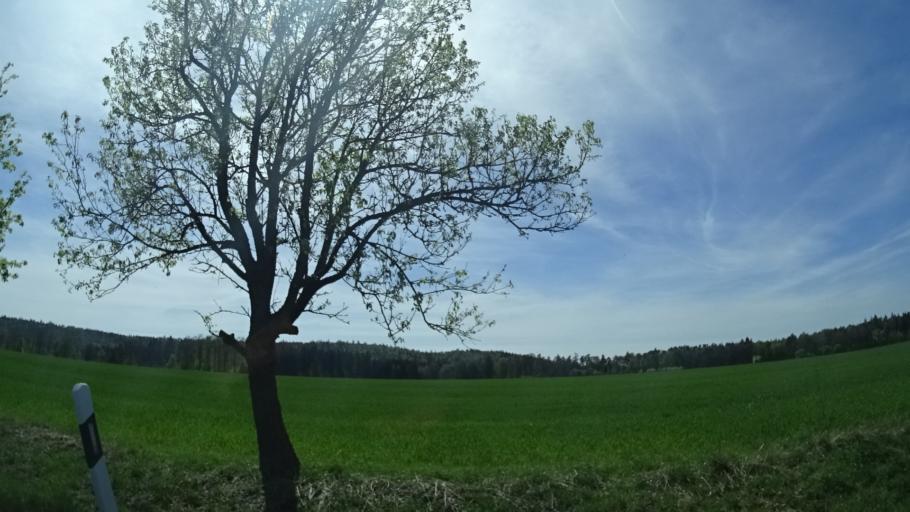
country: DE
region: Bavaria
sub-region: Regierungsbezirk Unterfranken
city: Ermershausen
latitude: 50.1814
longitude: 10.6236
